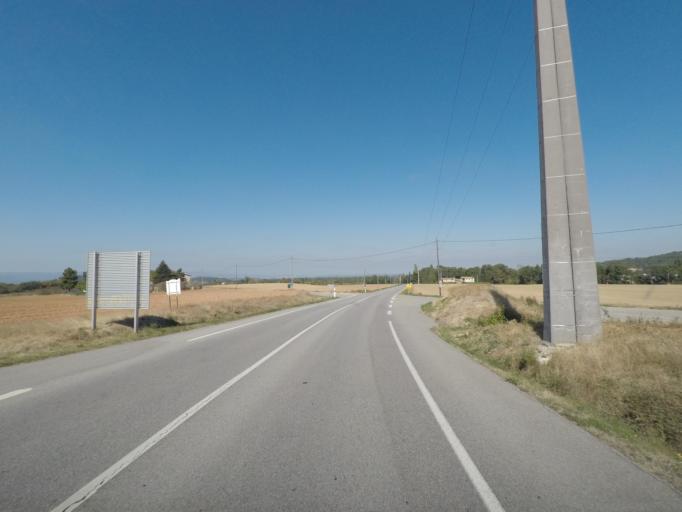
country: FR
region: Rhone-Alpes
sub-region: Departement de la Drome
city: Upie
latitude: 44.8210
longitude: 5.0104
